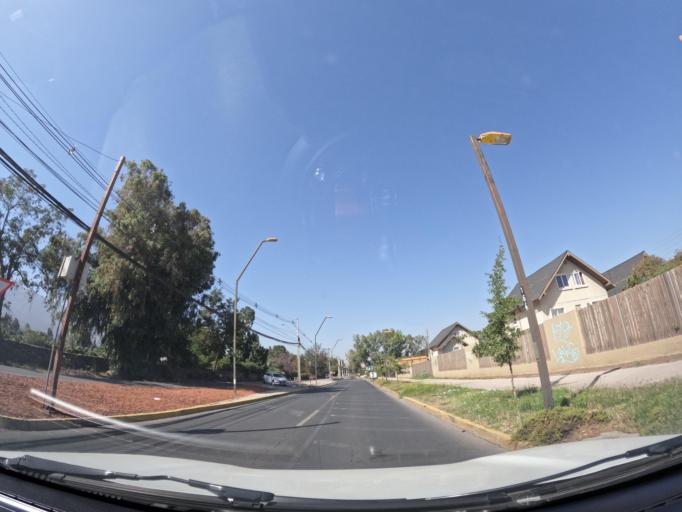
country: CL
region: Santiago Metropolitan
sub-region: Provincia de Santiago
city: Villa Presidente Frei, Nunoa, Santiago, Chile
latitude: -33.4984
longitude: -70.5521
